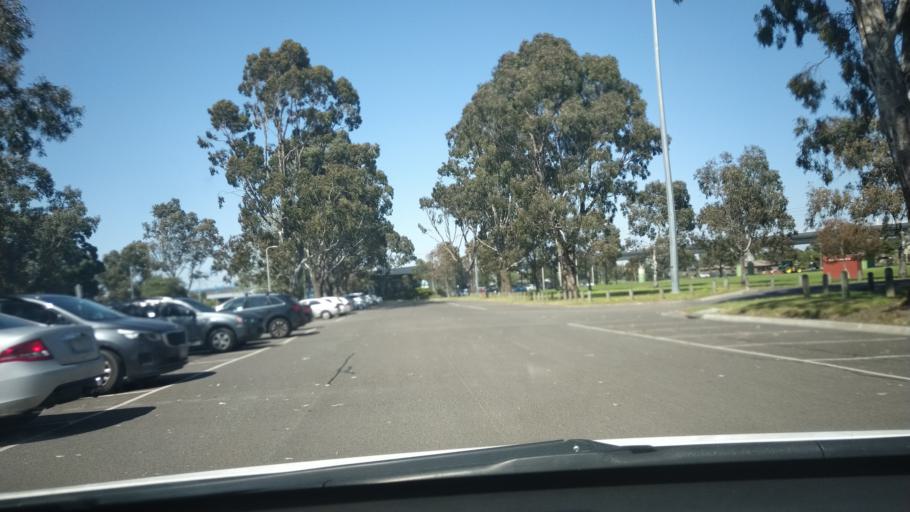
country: AU
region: Victoria
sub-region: Greater Dandenong
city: Noble Park
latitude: -37.9614
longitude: 145.1728
